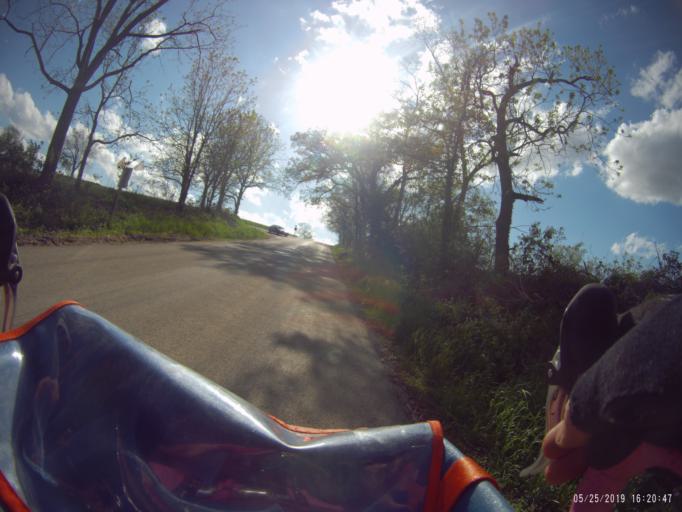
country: US
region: Wisconsin
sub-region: Dane County
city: Mount Horeb
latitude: 42.9664
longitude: -89.7006
